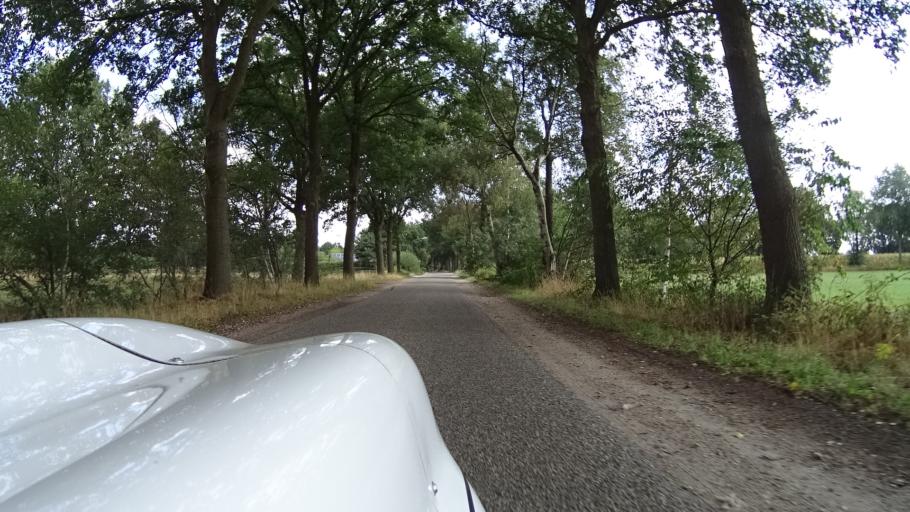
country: NL
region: North Brabant
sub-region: Gemeente Bernheze
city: Loosbroek
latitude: 51.6703
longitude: 5.4861
